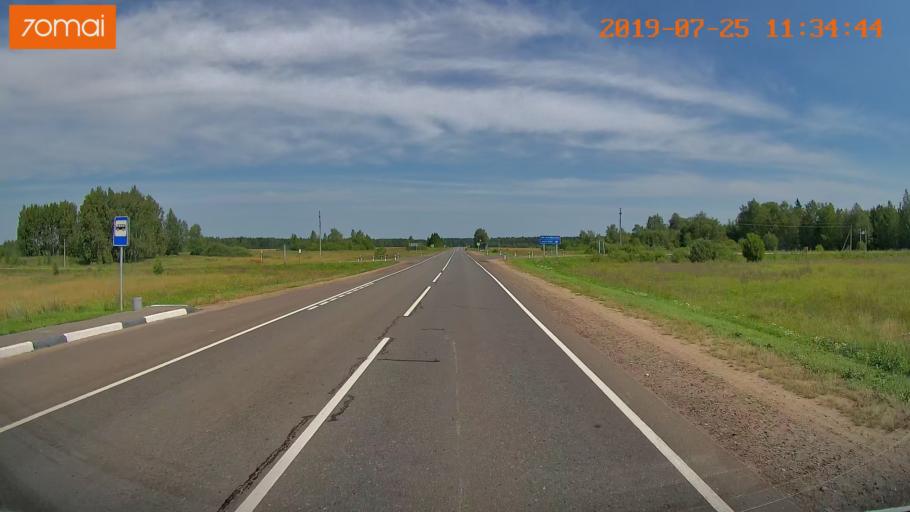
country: RU
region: Ivanovo
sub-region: Privolzhskiy Rayon
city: Ples
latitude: 57.4029
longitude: 41.4181
